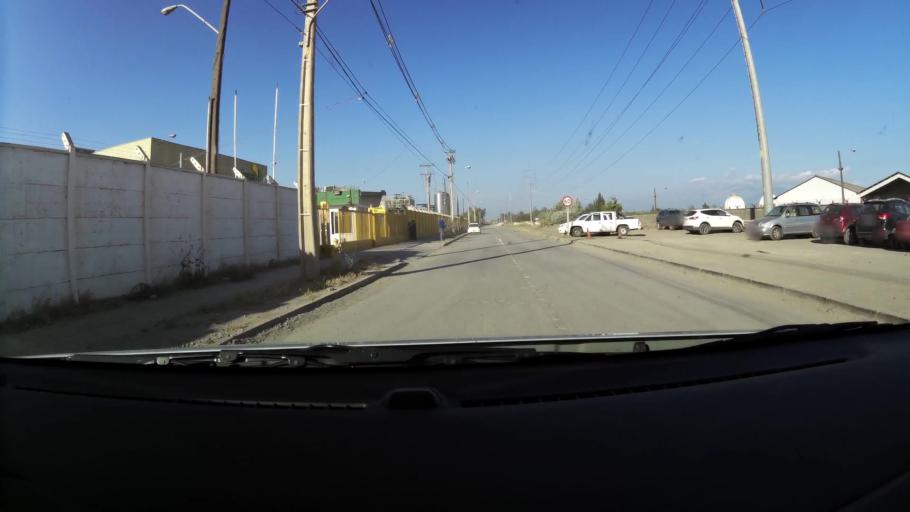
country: CL
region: Santiago Metropolitan
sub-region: Provincia de Maipo
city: San Bernardo
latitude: -33.5393
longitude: -70.7635
